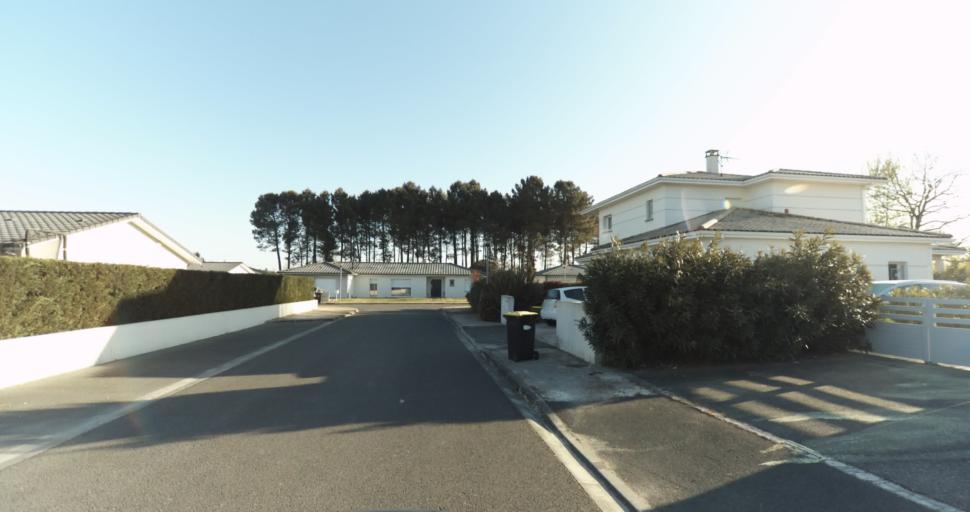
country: FR
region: Aquitaine
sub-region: Departement de la Gironde
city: Martignas-sur-Jalle
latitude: 44.8175
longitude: -0.7815
